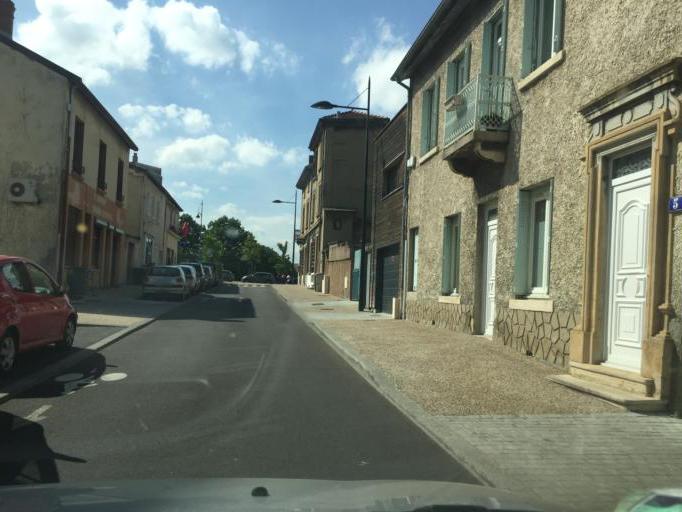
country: FR
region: Rhone-Alpes
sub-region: Departement du Rhone
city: Sathonay-Camp
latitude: 45.8217
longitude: 4.8733
